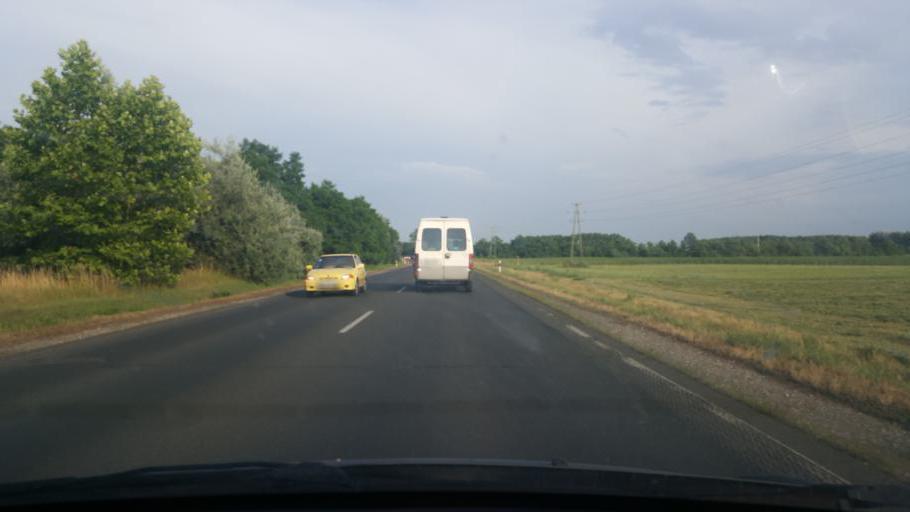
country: HU
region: Pest
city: Peteri
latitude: 47.3625
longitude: 19.3868
